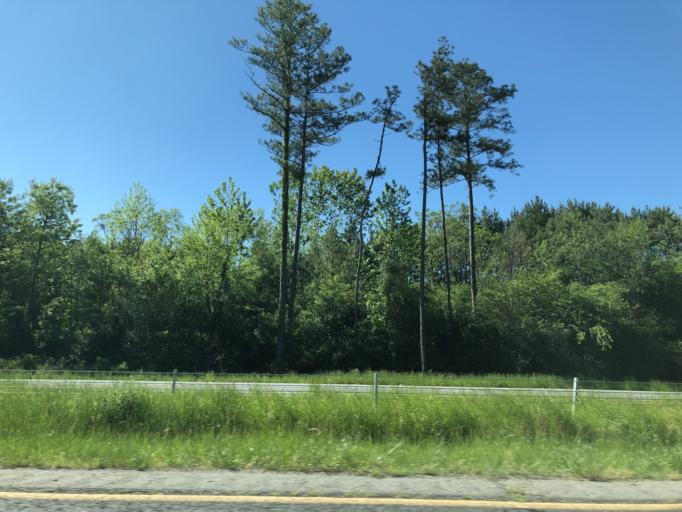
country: US
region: Georgia
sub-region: Clarke County
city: Country Club Estates
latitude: 33.9506
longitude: -83.4431
